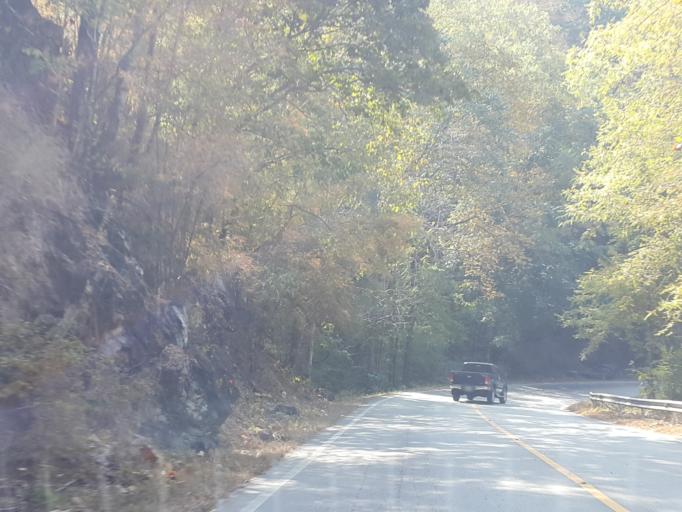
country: TH
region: Chiang Mai
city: Hot
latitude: 18.2274
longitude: 98.4499
